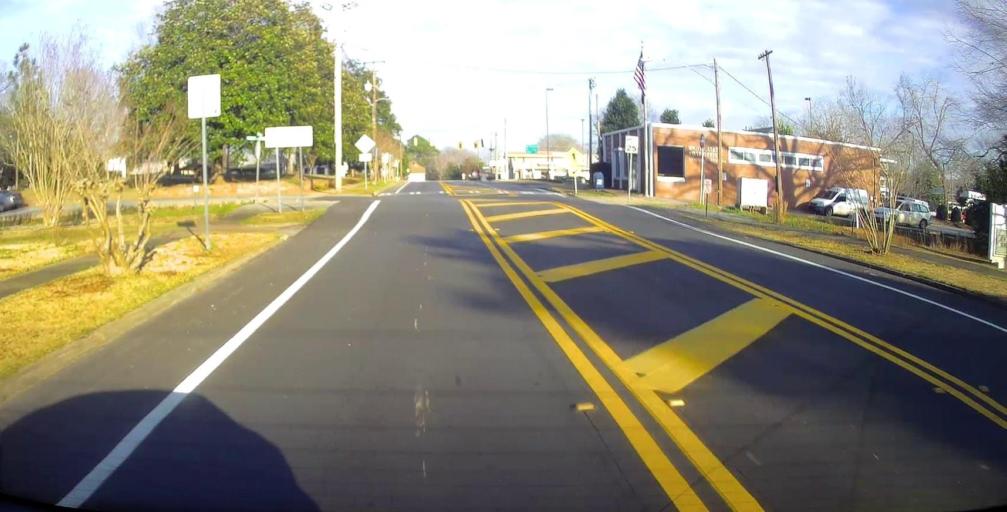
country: US
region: Georgia
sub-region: Harris County
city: Hamilton
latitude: 32.7579
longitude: -84.8761
